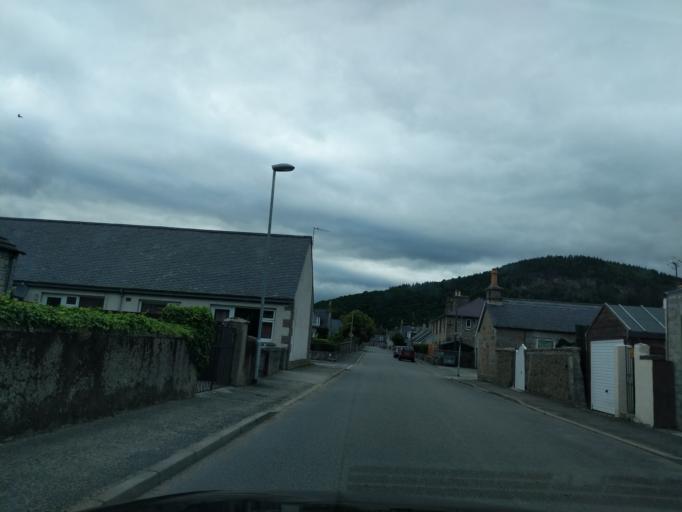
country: GB
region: Scotland
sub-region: Aberdeenshire
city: Ballater
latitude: 57.0461
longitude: -3.0401
